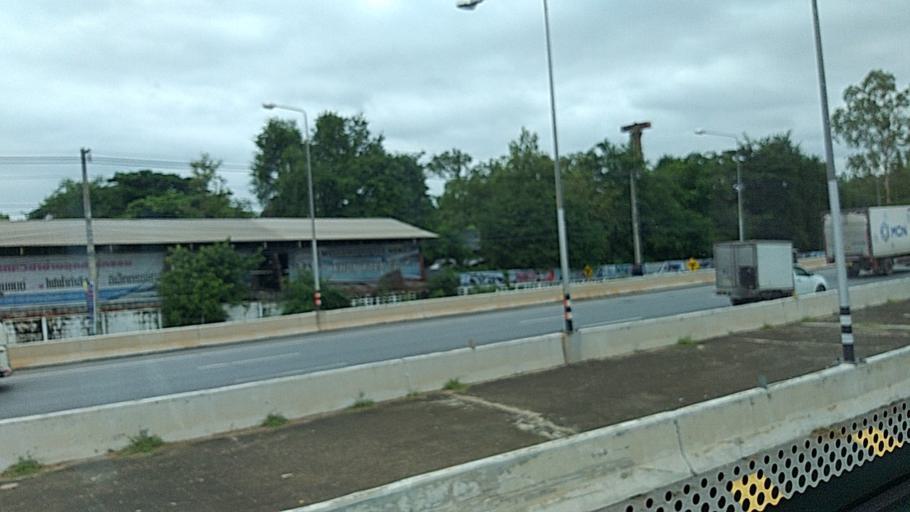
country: TH
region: Khon Kaen
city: Phon
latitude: 15.8266
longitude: 102.6079
